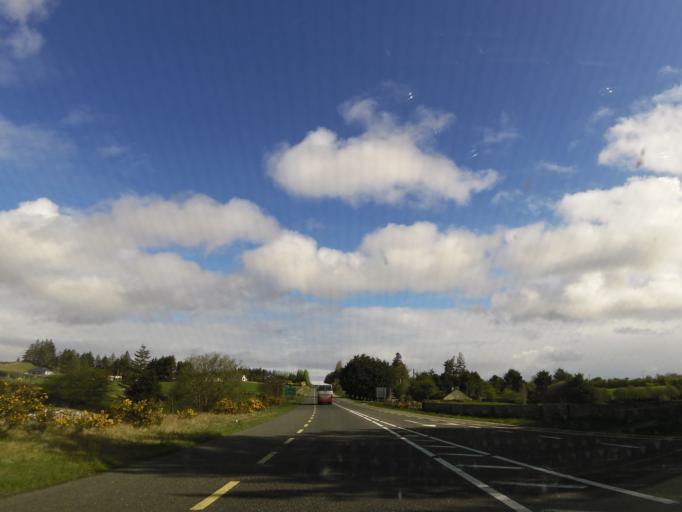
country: IE
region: Connaught
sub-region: Maigh Eo
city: Ballyhaunis
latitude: 53.8868
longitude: -8.8021
